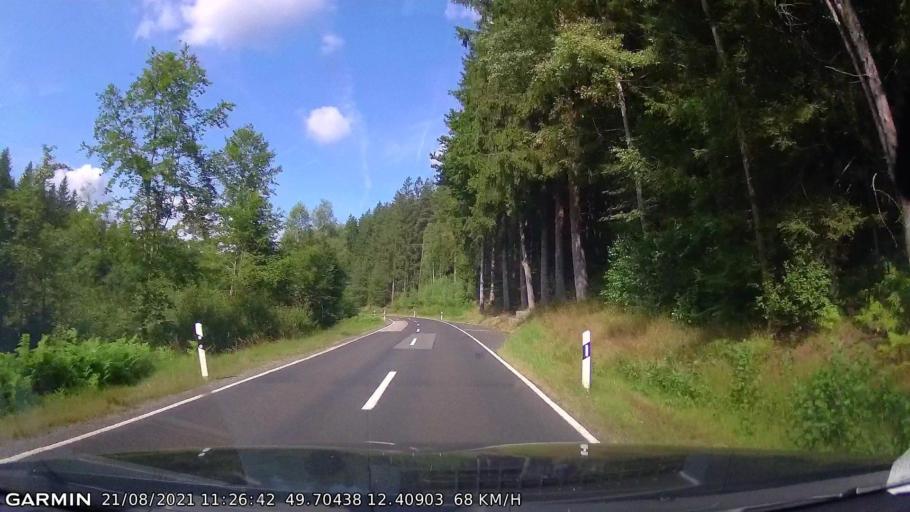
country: DE
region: Bavaria
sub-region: Upper Palatinate
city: Georgenberg
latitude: 49.7044
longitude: 12.4091
